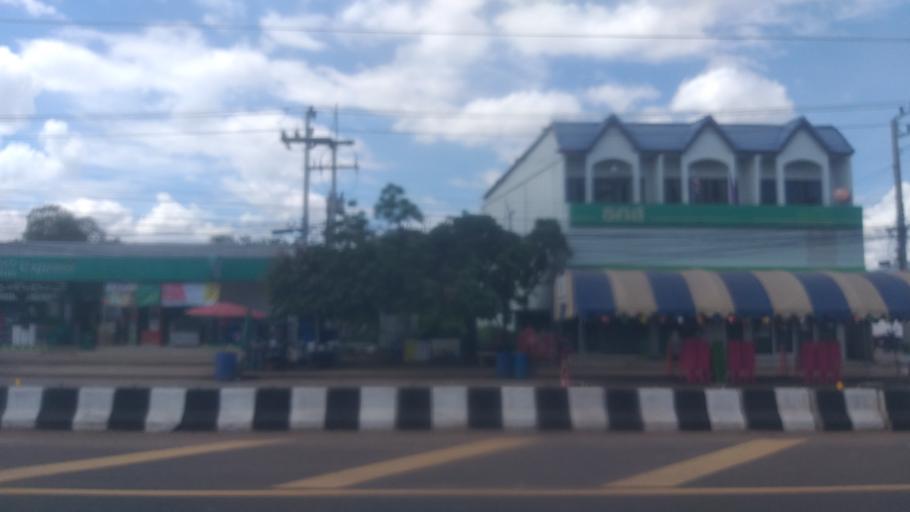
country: TH
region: Nakhon Ratchasima
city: Phra Thong Kham
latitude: 15.3099
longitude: 101.9673
